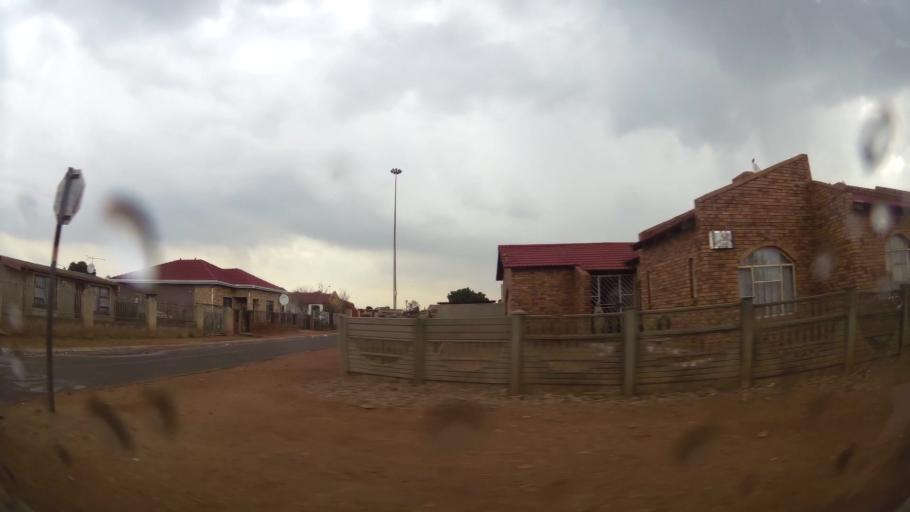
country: ZA
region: Gauteng
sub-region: Ekurhuleni Metropolitan Municipality
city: Germiston
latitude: -26.3619
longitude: 28.1648
